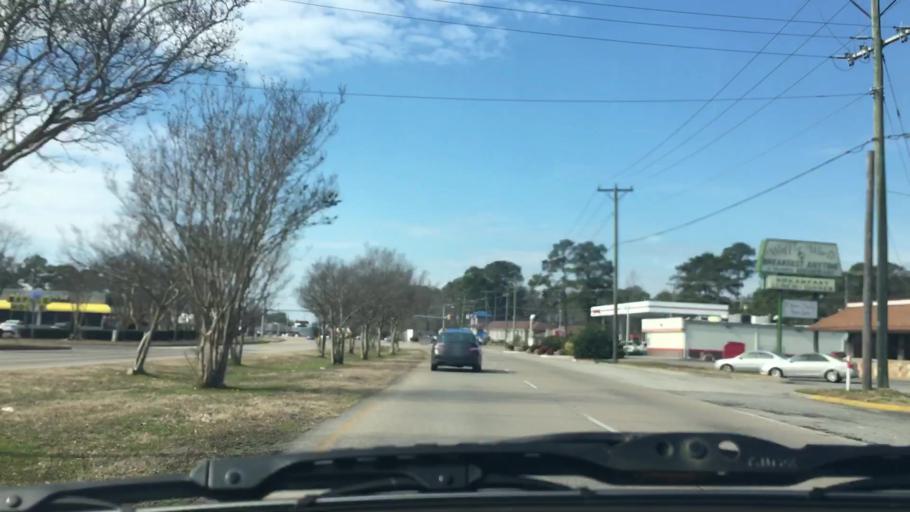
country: US
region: Virginia
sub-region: City of Portsmouth
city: Portsmouth Heights
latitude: 36.8648
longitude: -76.4081
